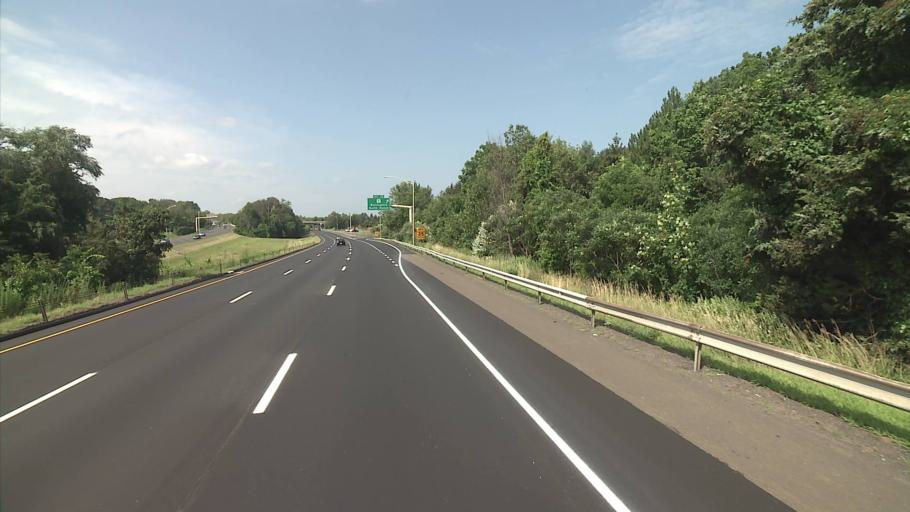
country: US
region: Connecticut
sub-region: New Haven County
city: Wallingford Center
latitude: 41.4257
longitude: -72.8210
